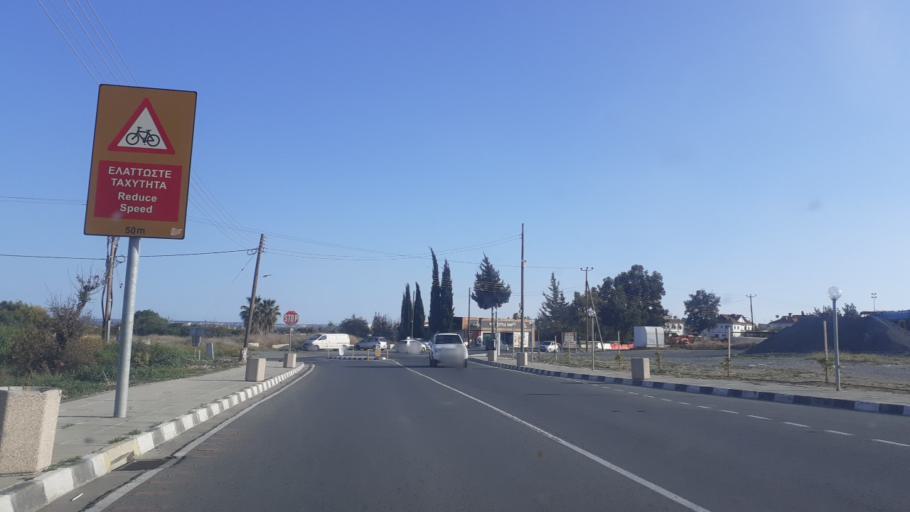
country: CY
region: Larnaka
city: Kolossi
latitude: 34.6769
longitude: 32.9432
